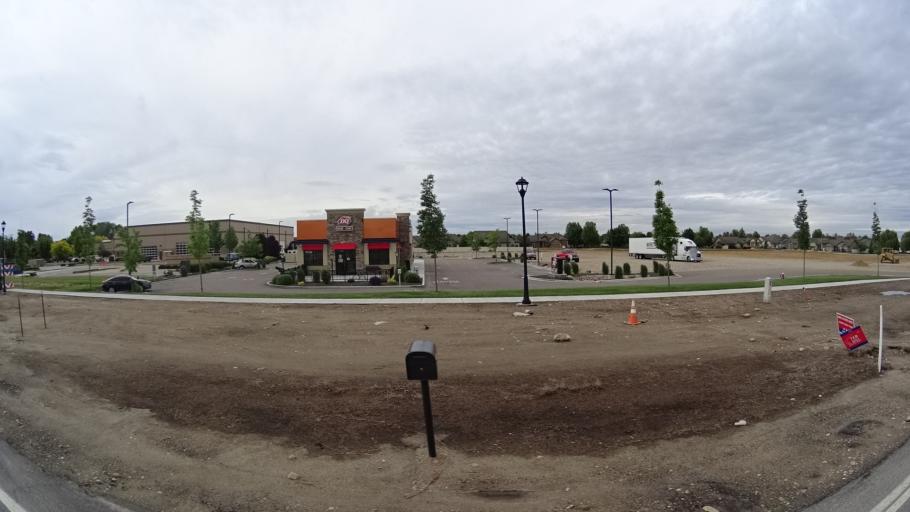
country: US
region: Idaho
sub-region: Ada County
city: Star
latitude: 43.6923
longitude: -116.4999
